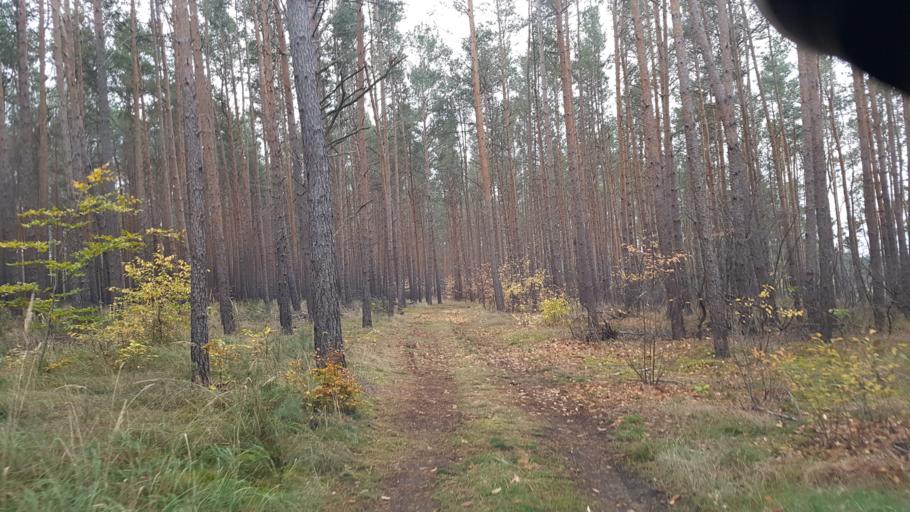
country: DE
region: Brandenburg
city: Finsterwalde
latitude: 51.5736
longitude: 13.6854
